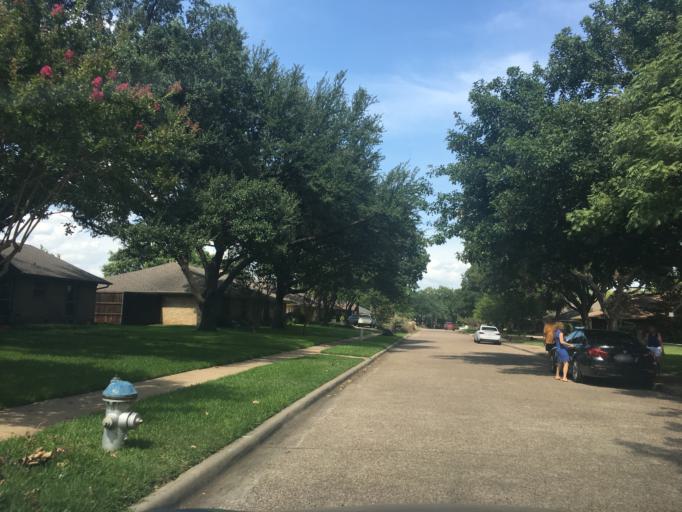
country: US
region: Texas
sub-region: Dallas County
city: Addison
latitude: 32.9210
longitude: -96.8365
